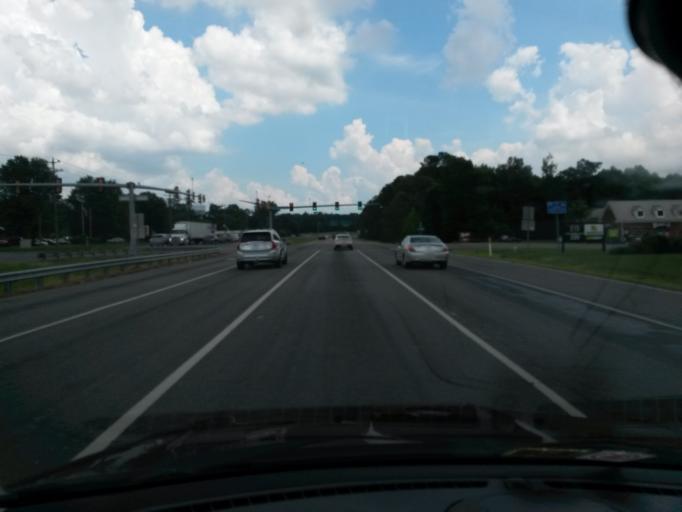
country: US
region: Virginia
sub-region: Chesterfield County
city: Enon
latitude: 37.3460
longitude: -77.3435
